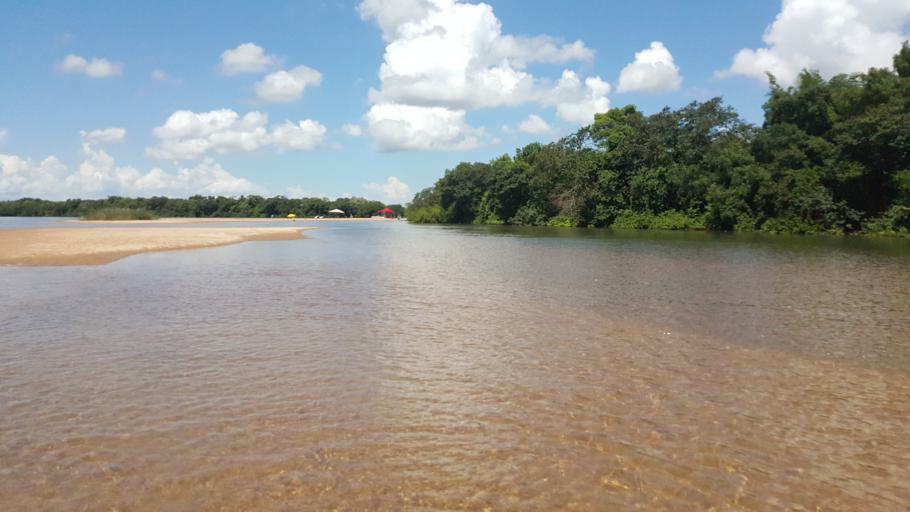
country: AR
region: Corrientes
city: Ituzaingo
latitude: -27.5756
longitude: -56.7076
